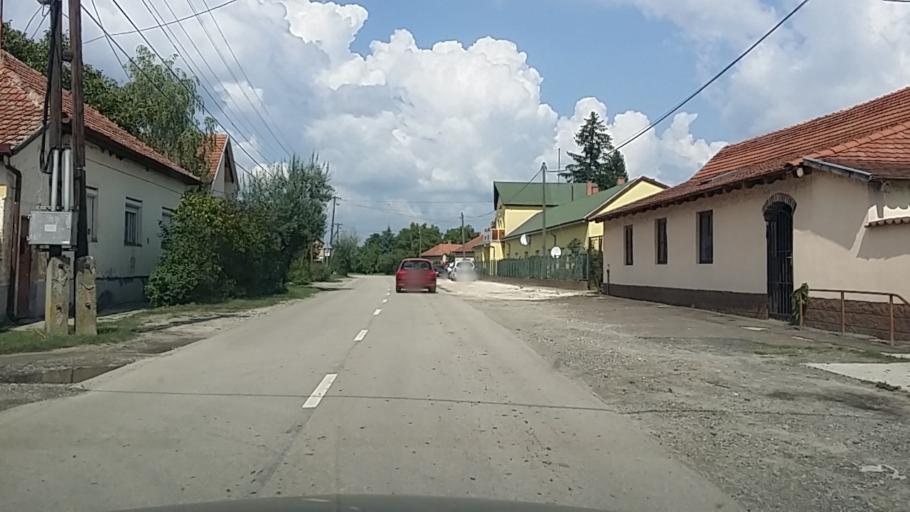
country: HU
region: Bacs-Kiskun
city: Tiszaalpar
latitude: 46.8018
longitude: 20.0075
